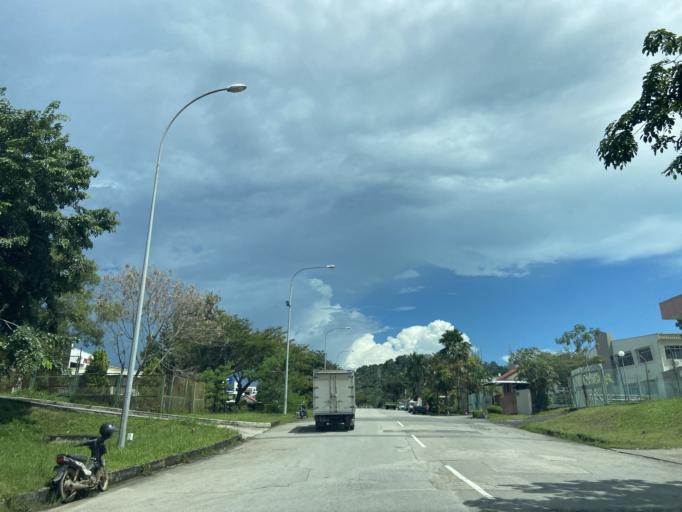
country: SG
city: Singapore
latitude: 1.0567
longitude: 104.0378
